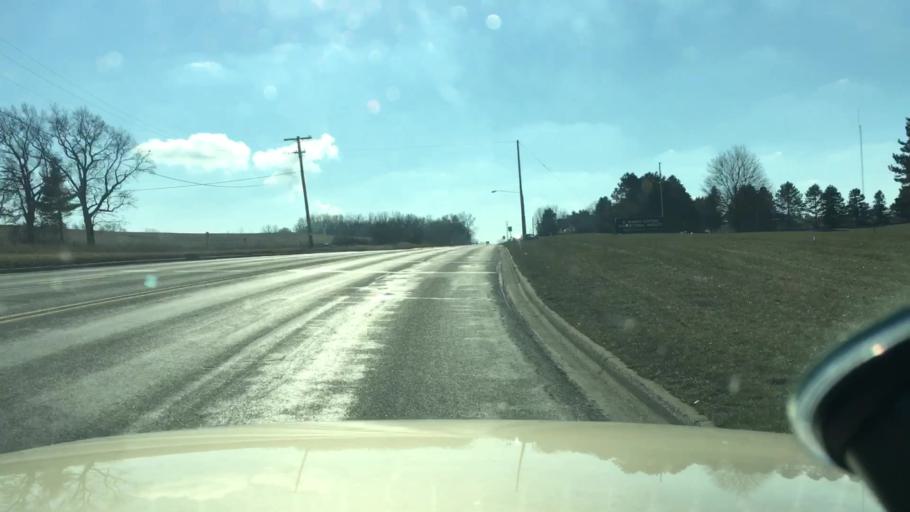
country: US
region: Michigan
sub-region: Jackson County
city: Jackson
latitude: 42.2886
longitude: -84.3844
